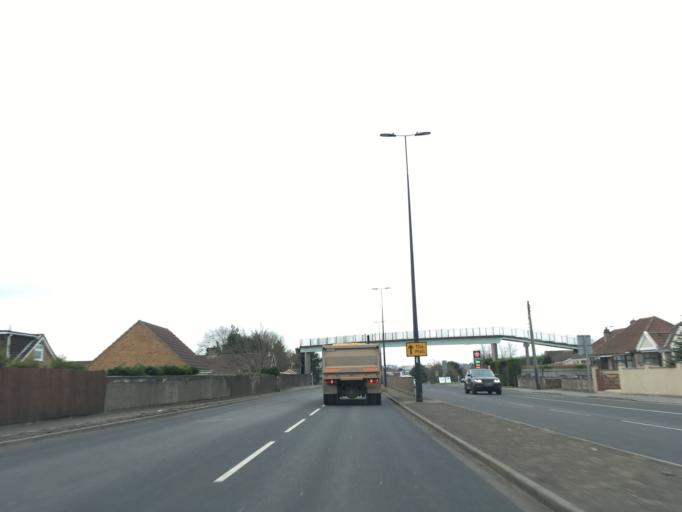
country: GB
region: England
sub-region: South Gloucestershire
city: Almondsbury
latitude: 51.5375
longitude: -2.5667
